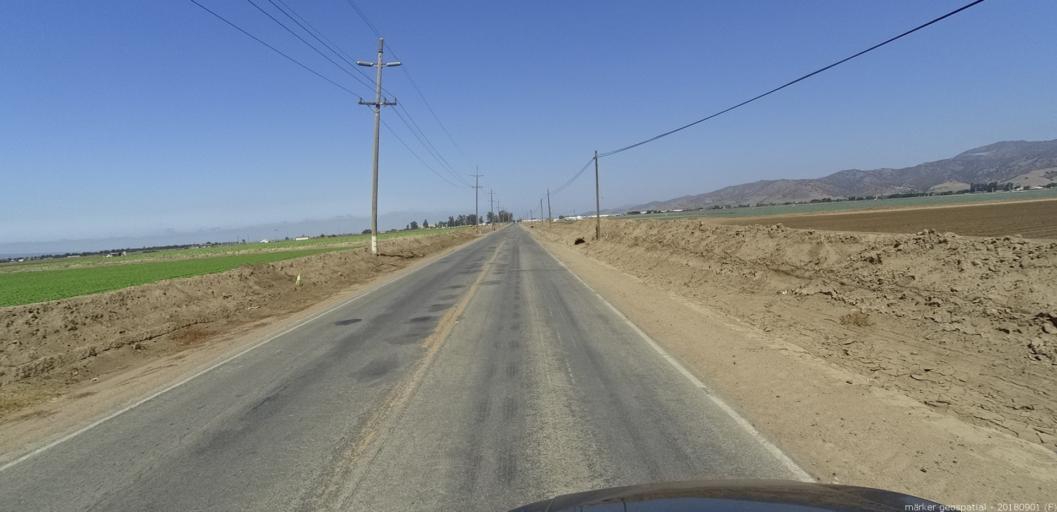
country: US
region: California
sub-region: Monterey County
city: Chualar
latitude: 36.6037
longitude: -121.5128
